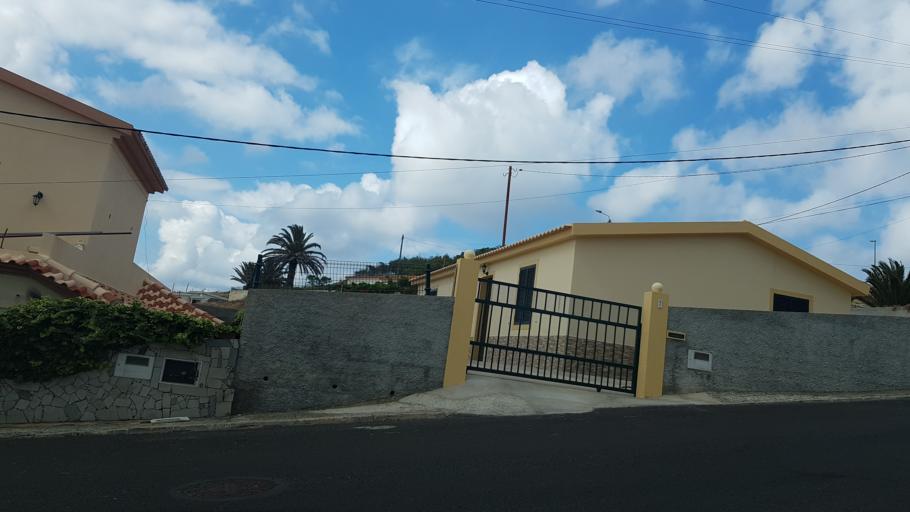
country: PT
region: Madeira
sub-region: Porto Santo
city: Vila de Porto Santo
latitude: 33.0397
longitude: -16.3617
